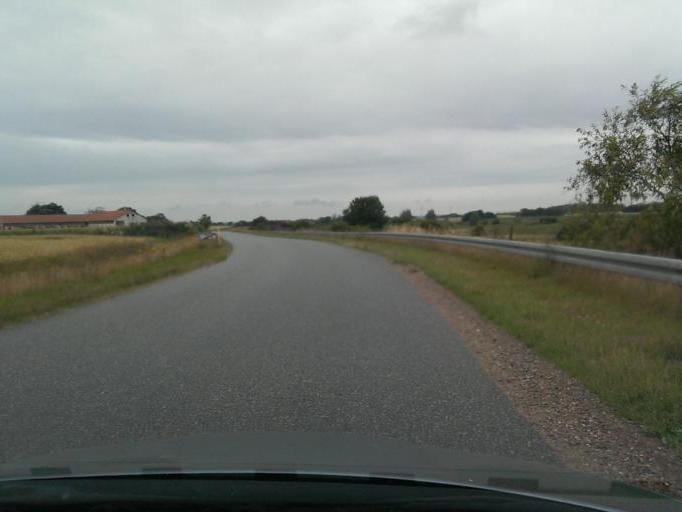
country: DK
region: North Denmark
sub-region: Hjorring Kommune
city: Vra
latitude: 57.3544
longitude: 9.9307
